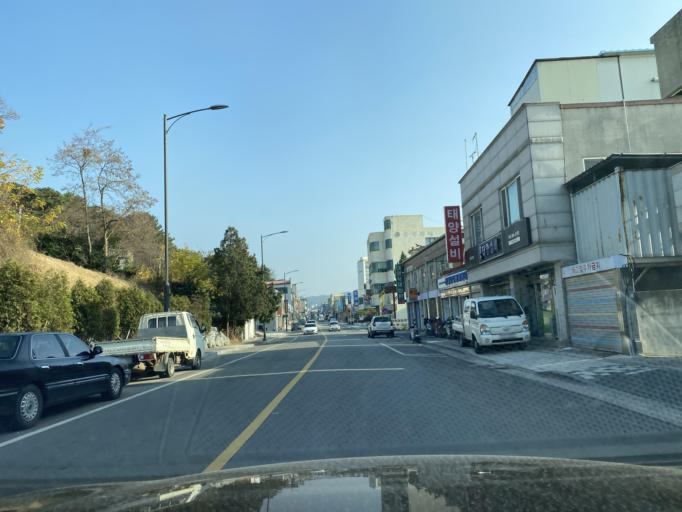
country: KR
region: Chungcheongnam-do
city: Yesan
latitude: 36.6808
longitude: 126.8339
